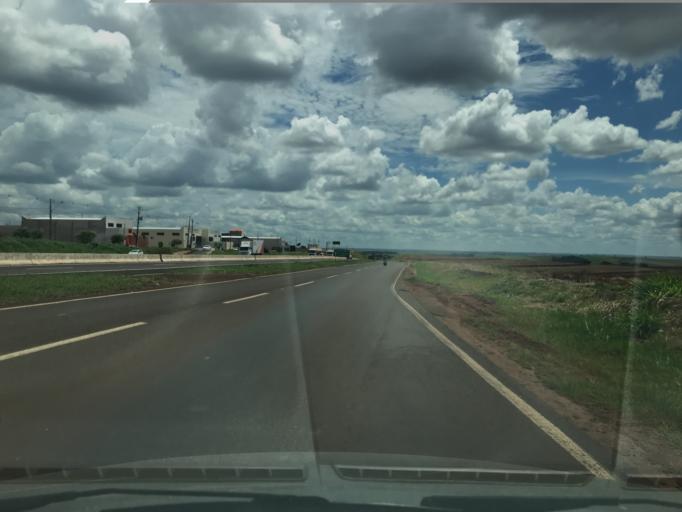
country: BR
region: Parana
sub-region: Maringa
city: Maringa
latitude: -23.3785
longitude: -51.9147
